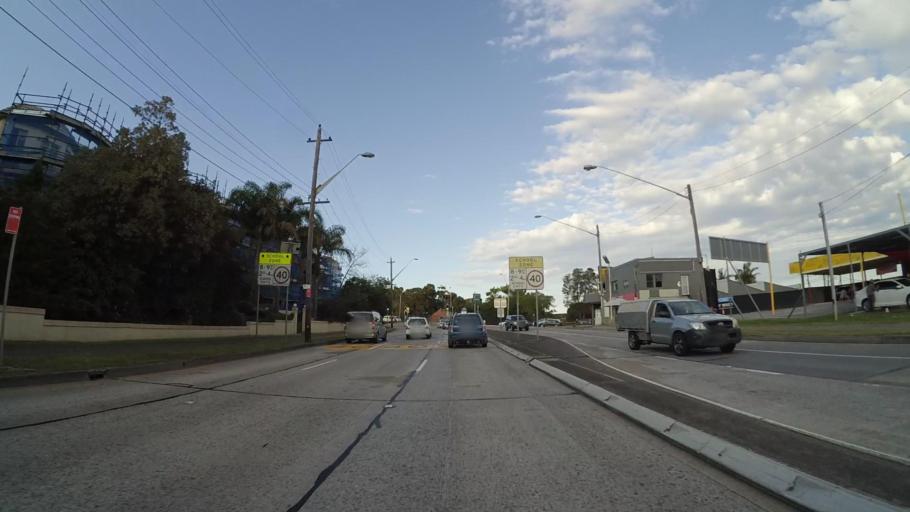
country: AU
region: New South Wales
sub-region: Kogarah
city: Beverly Park
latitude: -33.9695
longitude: 151.1354
